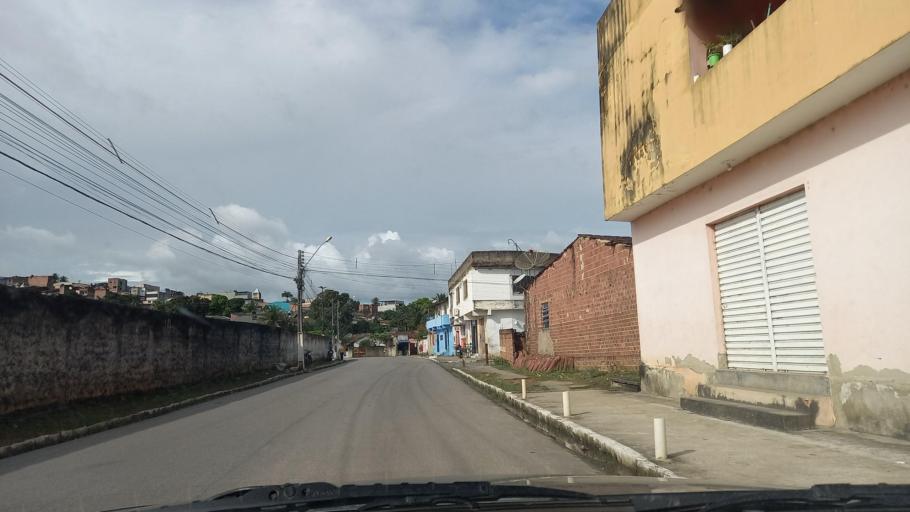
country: BR
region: Pernambuco
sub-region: Palmares
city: Palmares
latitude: -8.6823
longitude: -35.5956
